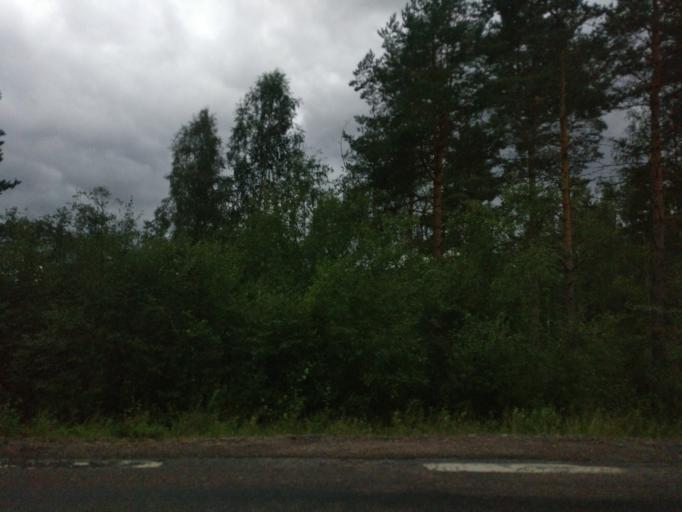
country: SE
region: Vaermland
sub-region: Torsby Kommun
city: Torsby
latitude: 60.5972
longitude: 13.0698
